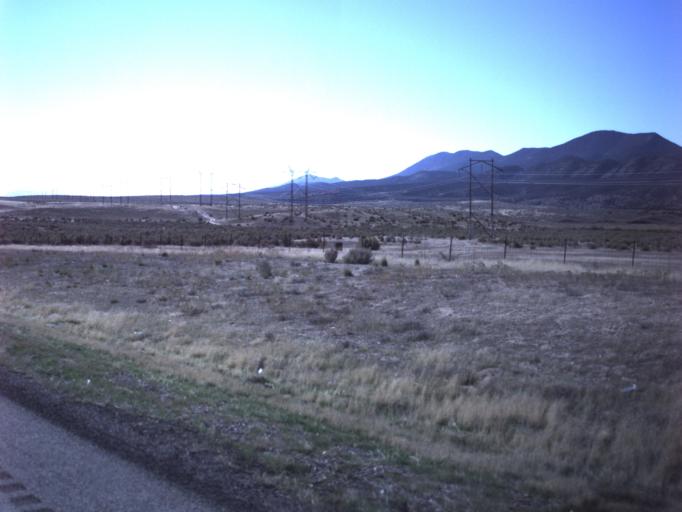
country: US
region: Utah
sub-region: Sanpete County
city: Gunnison
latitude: 39.3489
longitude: -111.9276
